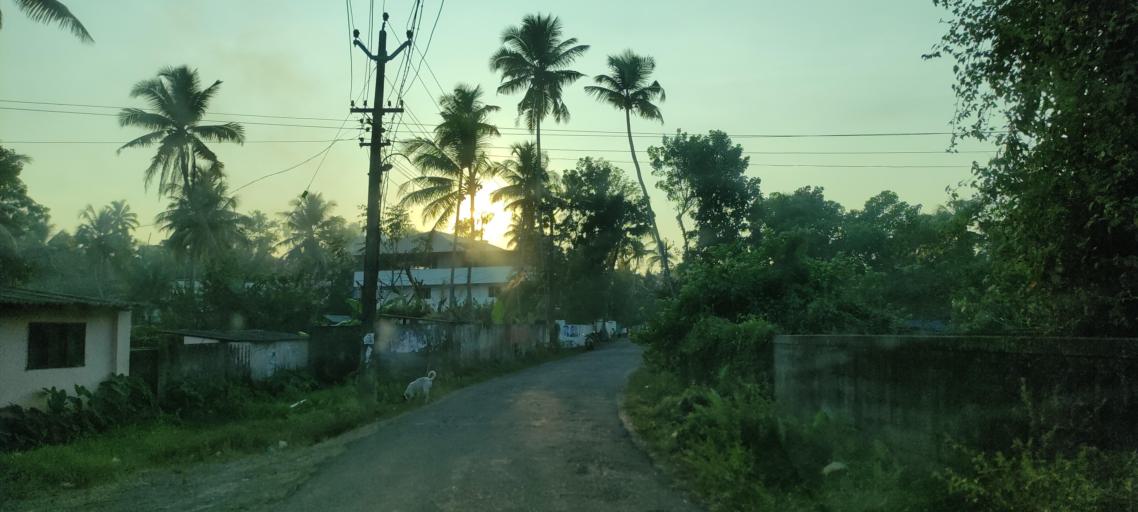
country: IN
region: Kerala
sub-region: Alappuzha
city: Kutiatodu
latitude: 9.7876
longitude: 76.3208
